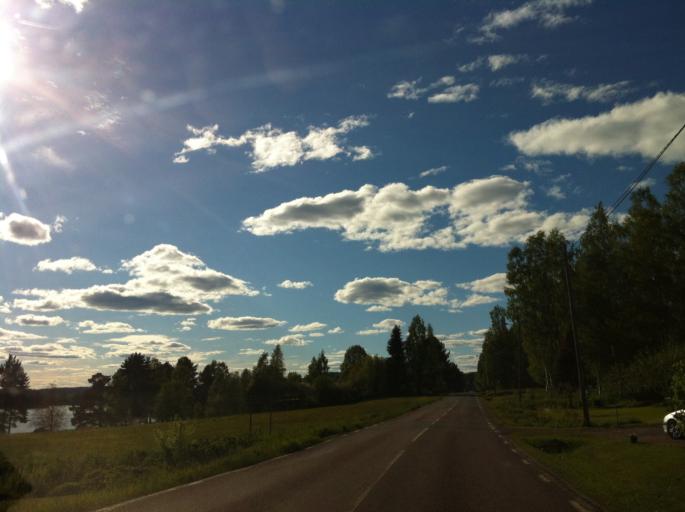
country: SE
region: Dalarna
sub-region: Leksand Municipality
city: Siljansnas
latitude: 60.7638
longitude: 14.9211
